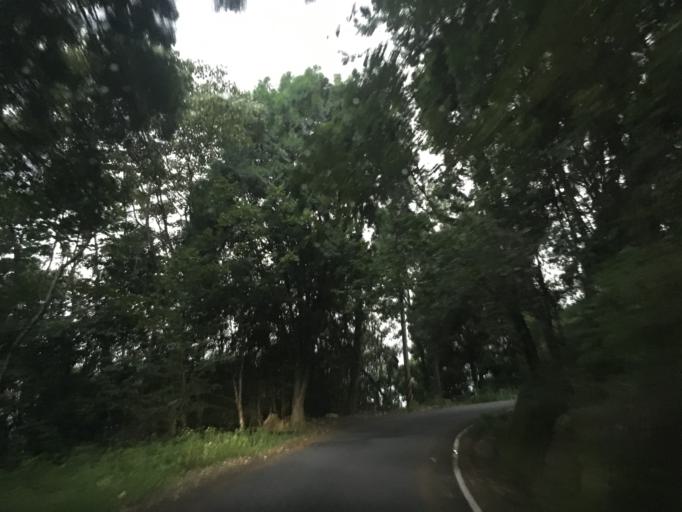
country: TW
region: Taiwan
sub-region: Nantou
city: Puli
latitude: 23.9046
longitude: 120.9085
